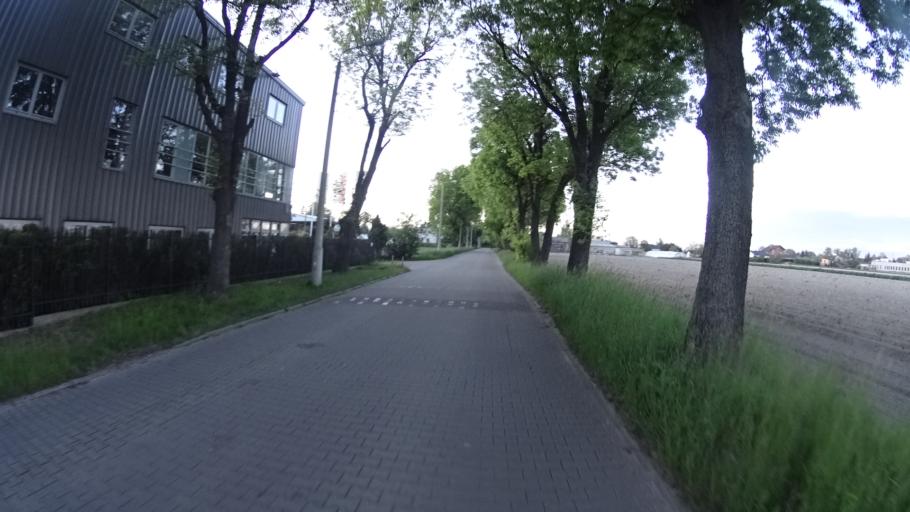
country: PL
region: Masovian Voivodeship
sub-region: Powiat warszawski zachodni
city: Ozarow Mazowiecki
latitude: 52.2087
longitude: 20.7556
